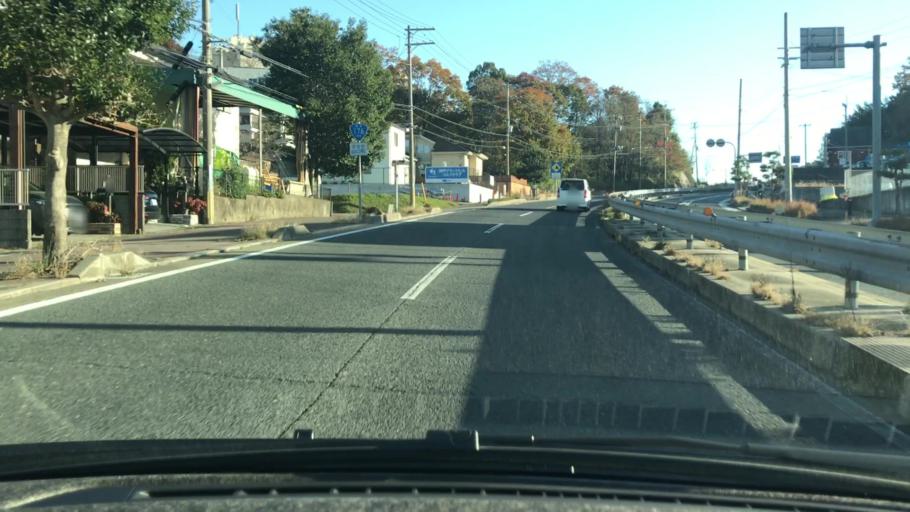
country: JP
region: Hyogo
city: Sandacho
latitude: 34.8308
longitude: 135.2522
